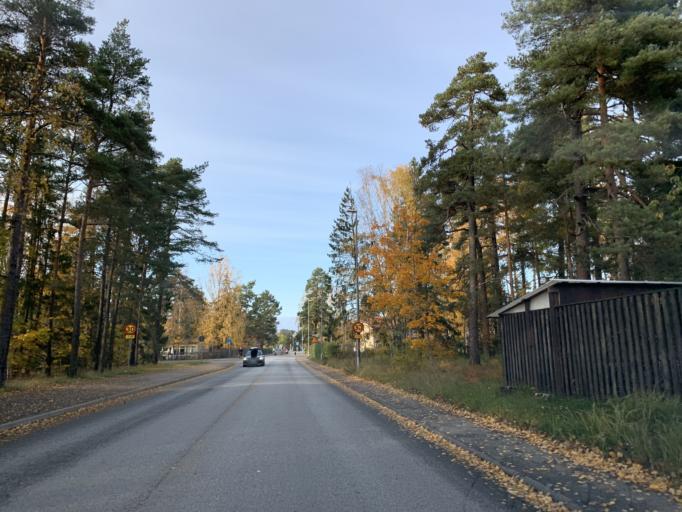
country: SE
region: Stockholm
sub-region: Haninge Kommun
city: Haninge
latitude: 59.1780
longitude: 18.1825
